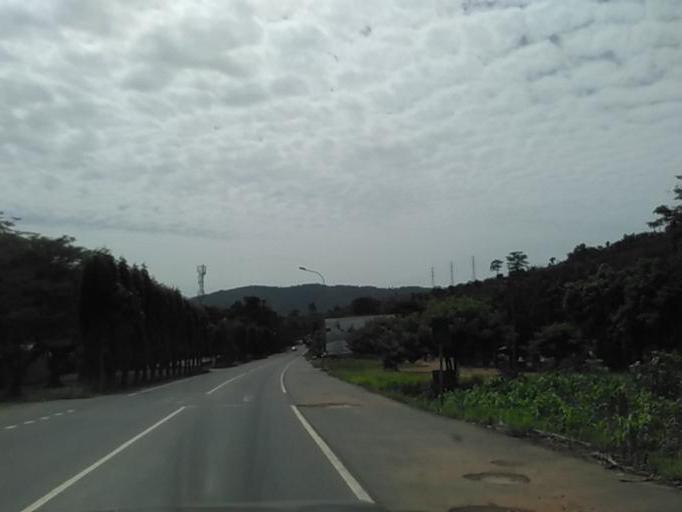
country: GH
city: Akropong
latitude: 6.2668
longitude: 0.0667
